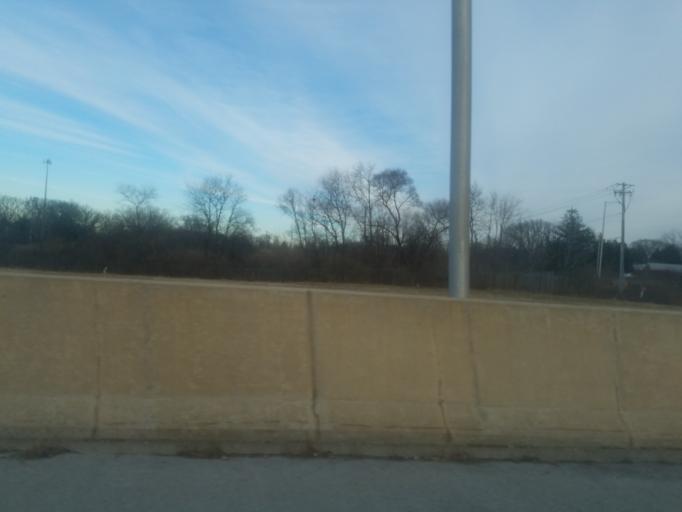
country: US
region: Illinois
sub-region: Cook County
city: Lemont
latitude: 41.6365
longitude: -88.0112
